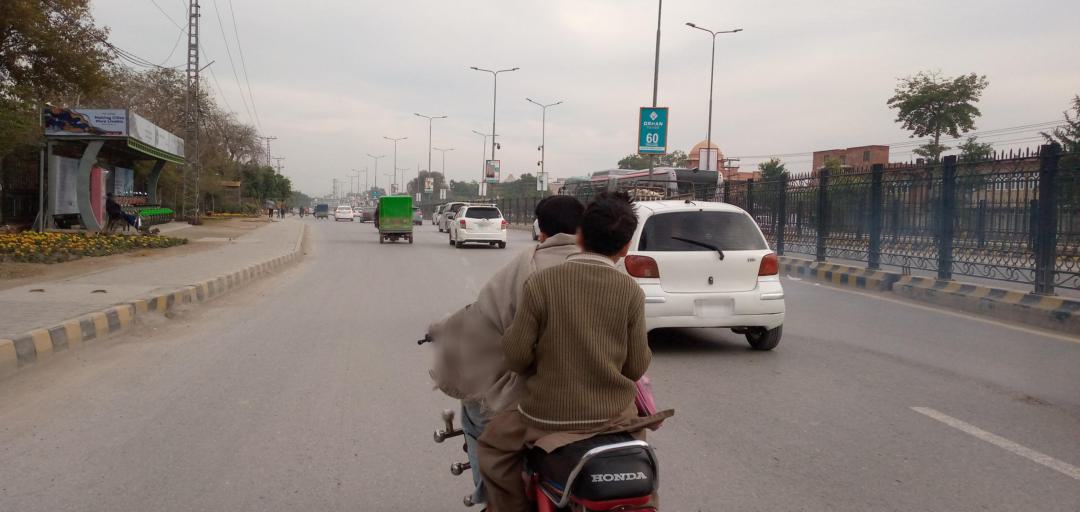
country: PK
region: Khyber Pakhtunkhwa
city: Peshawar
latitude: 33.9984
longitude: 71.4792
